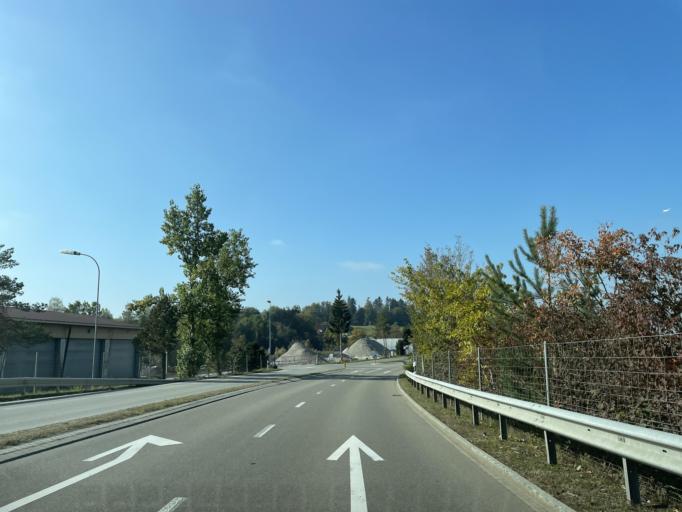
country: CH
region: Zurich
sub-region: Bezirk Buelach
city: Bassersdorf
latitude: 47.4356
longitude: 8.6257
